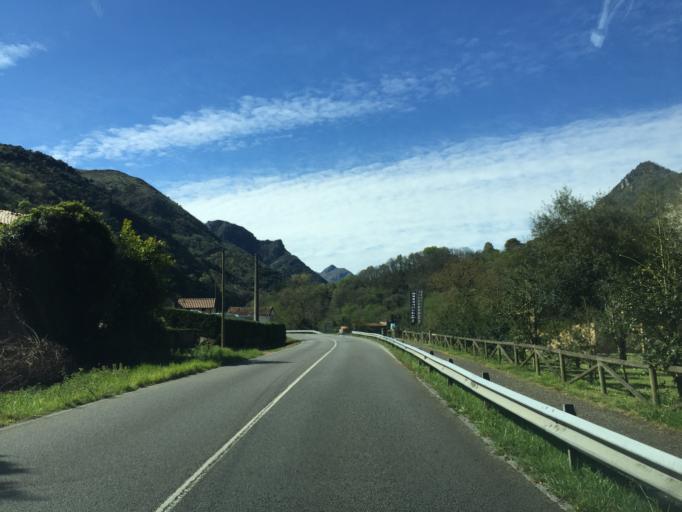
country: ES
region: Asturias
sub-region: Province of Asturias
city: Proaza
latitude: 43.2924
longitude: -5.9819
